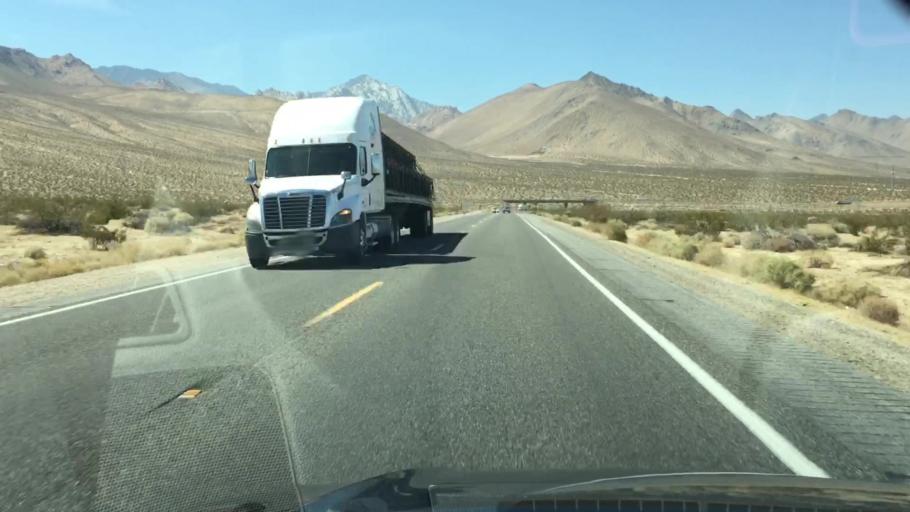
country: US
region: California
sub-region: Kern County
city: Inyokern
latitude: 35.6947
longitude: -117.8646
